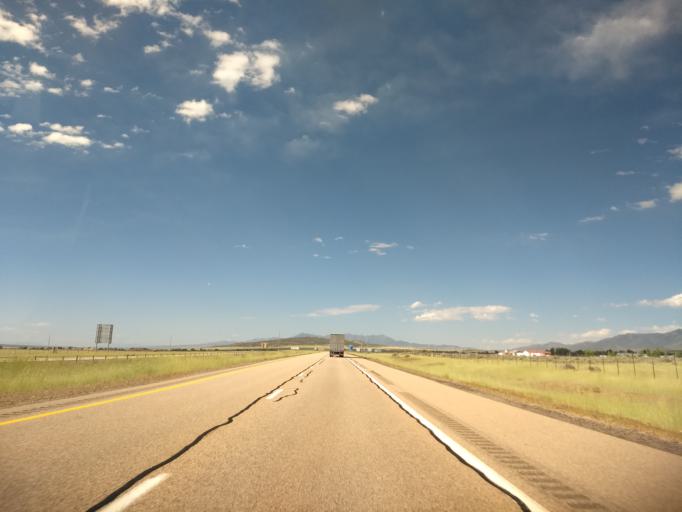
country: US
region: Utah
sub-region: Millard County
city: Fillmore
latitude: 38.9660
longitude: -112.3436
